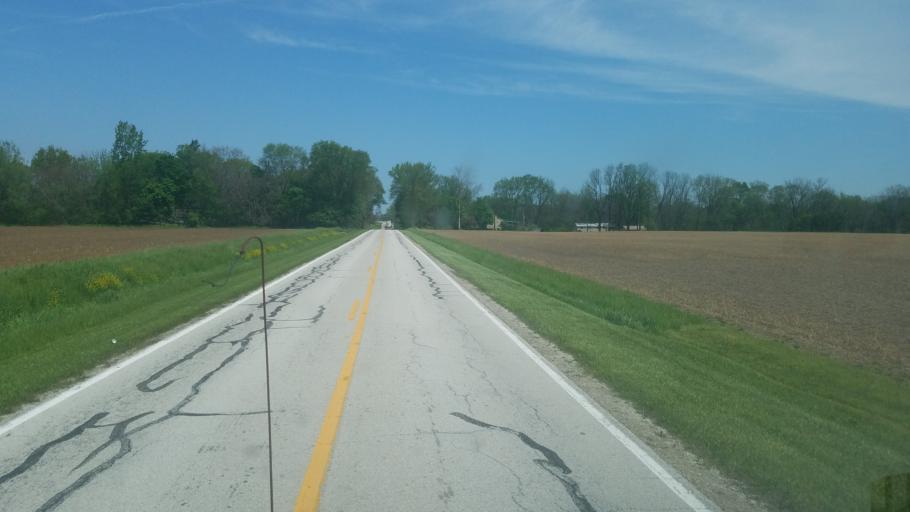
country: US
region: Ohio
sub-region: Sandusky County
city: Stony Prairie
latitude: 41.4197
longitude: -83.2017
